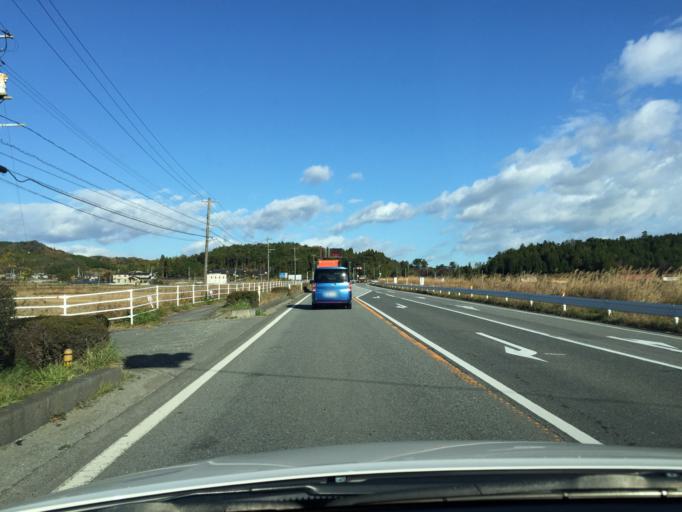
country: JP
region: Fukushima
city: Namie
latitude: 37.3020
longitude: 140.9940
